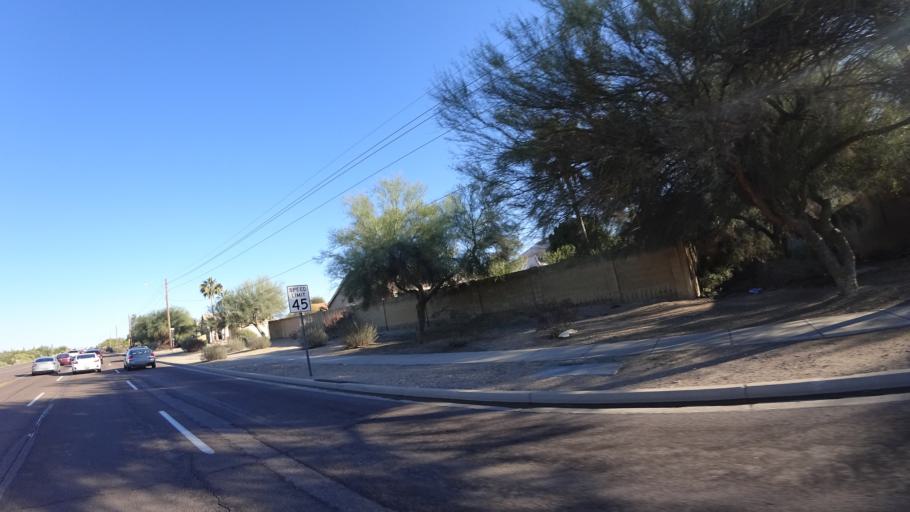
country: US
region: Arizona
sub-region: Maricopa County
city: Sun City
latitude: 33.7122
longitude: -112.1956
